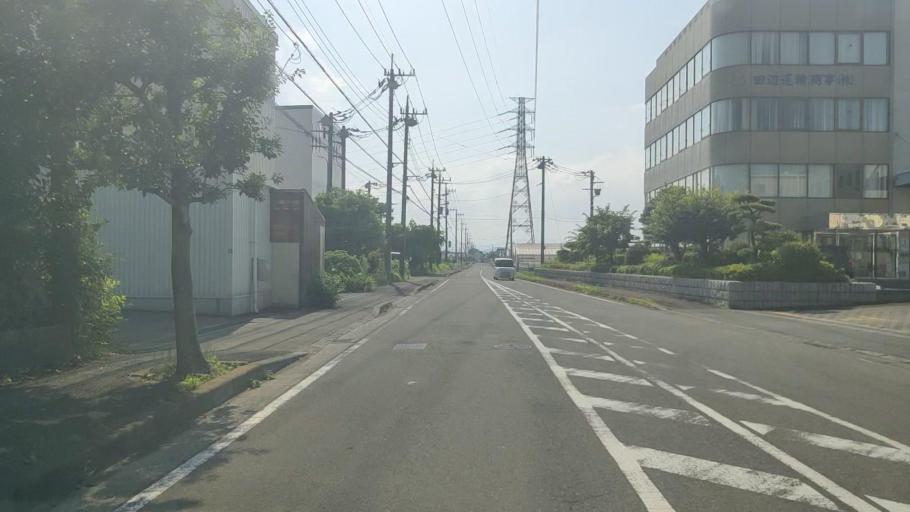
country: JP
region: Kanagawa
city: Hiratsuka
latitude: 35.3592
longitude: 139.3397
